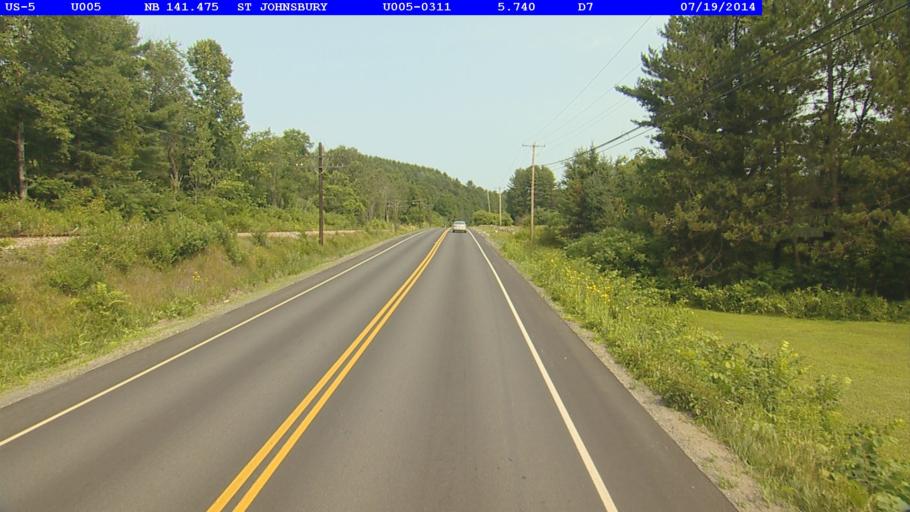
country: US
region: Vermont
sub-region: Caledonia County
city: Lyndon
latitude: 44.4734
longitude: -72.0151
